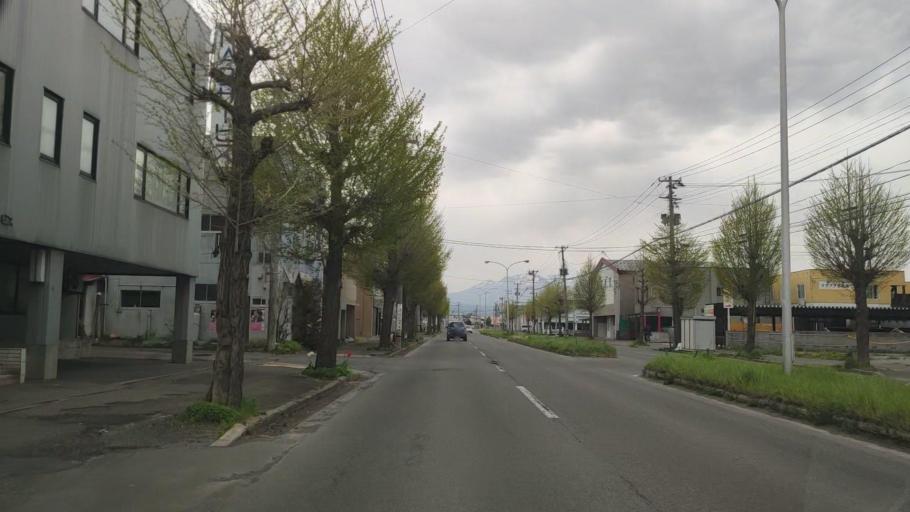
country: JP
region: Aomori
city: Aomori Shi
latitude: 40.8201
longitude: 140.7725
